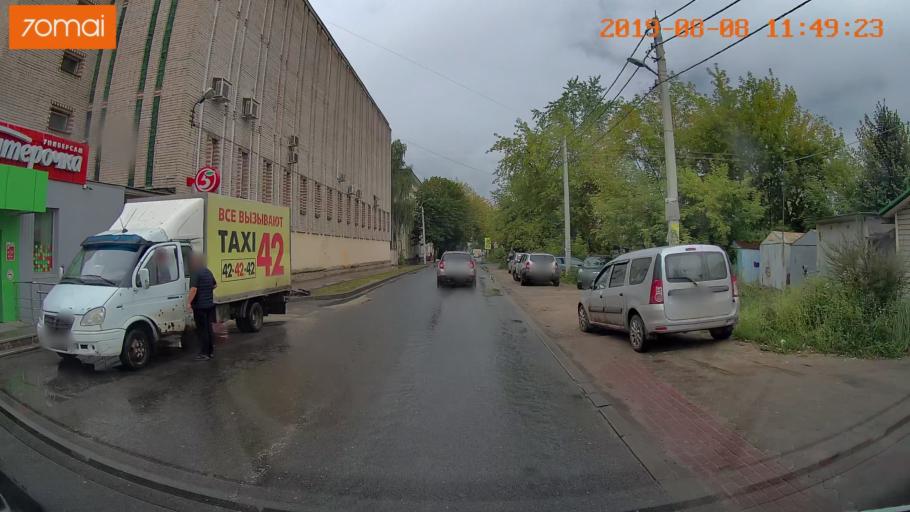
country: RU
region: Ivanovo
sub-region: Gorod Ivanovo
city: Ivanovo
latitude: 56.9777
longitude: 40.9810
